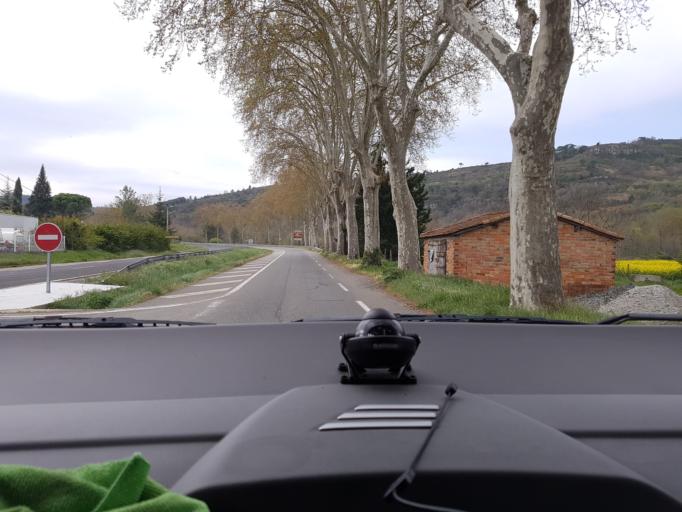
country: FR
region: Languedoc-Roussillon
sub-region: Departement de l'Aude
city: Couiza
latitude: 42.9538
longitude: 2.2550
